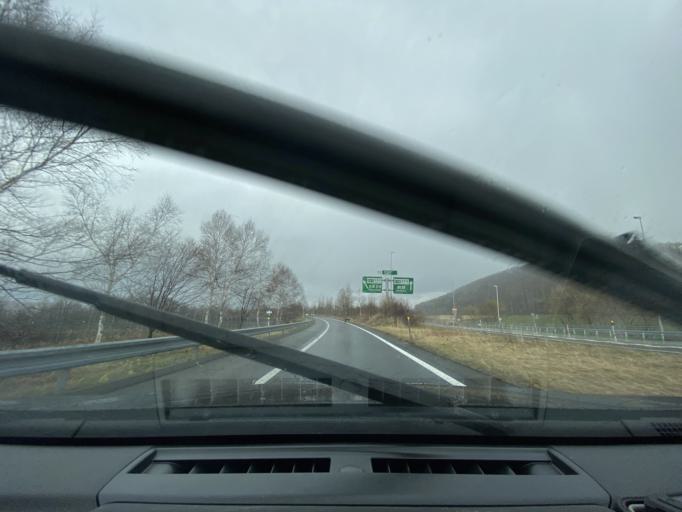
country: JP
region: Hokkaido
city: Otofuke
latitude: 43.1025
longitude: 143.5527
